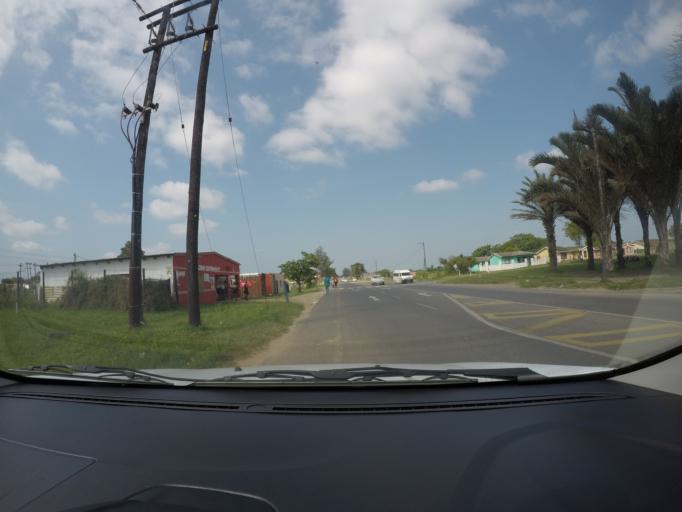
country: ZA
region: KwaZulu-Natal
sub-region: uThungulu District Municipality
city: eSikhawini
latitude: -28.8856
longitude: 31.9001
